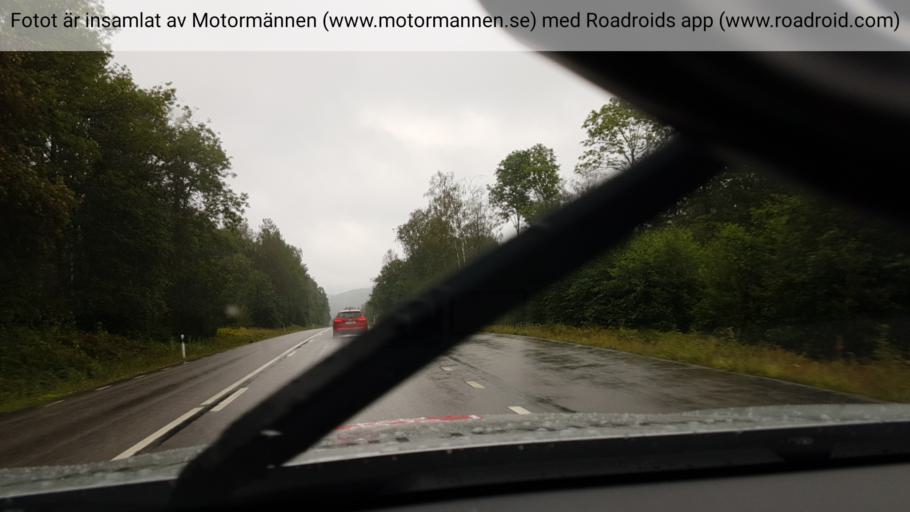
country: SE
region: Vaestra Goetaland
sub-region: Bengtsfors Kommun
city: Dals Langed
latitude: 59.0357
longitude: 12.4237
